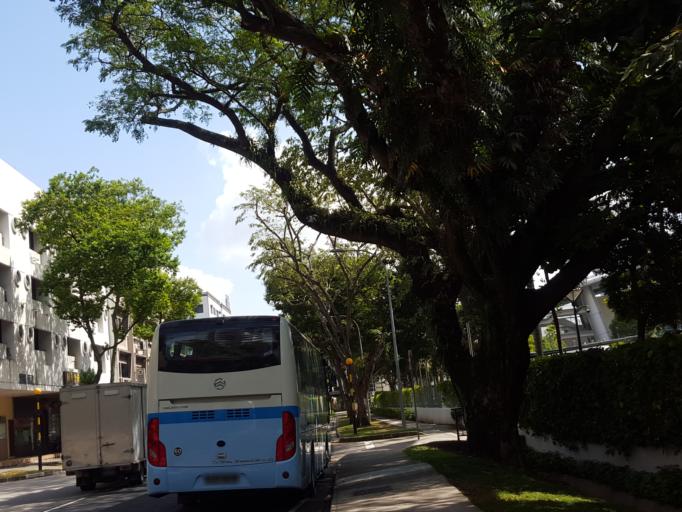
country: SG
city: Singapore
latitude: 1.3091
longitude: 103.8588
